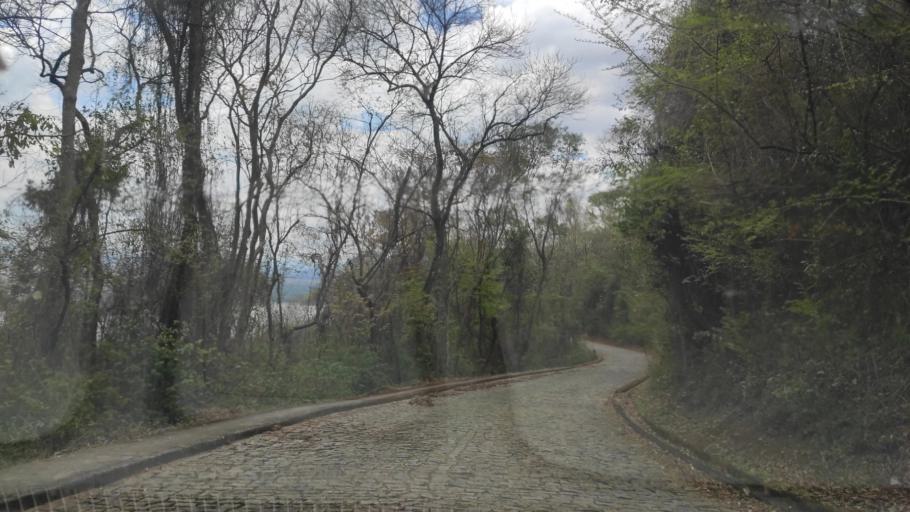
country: BR
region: Espirito Santo
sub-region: Vitoria
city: Vitoria
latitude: -20.3017
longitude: -40.3391
